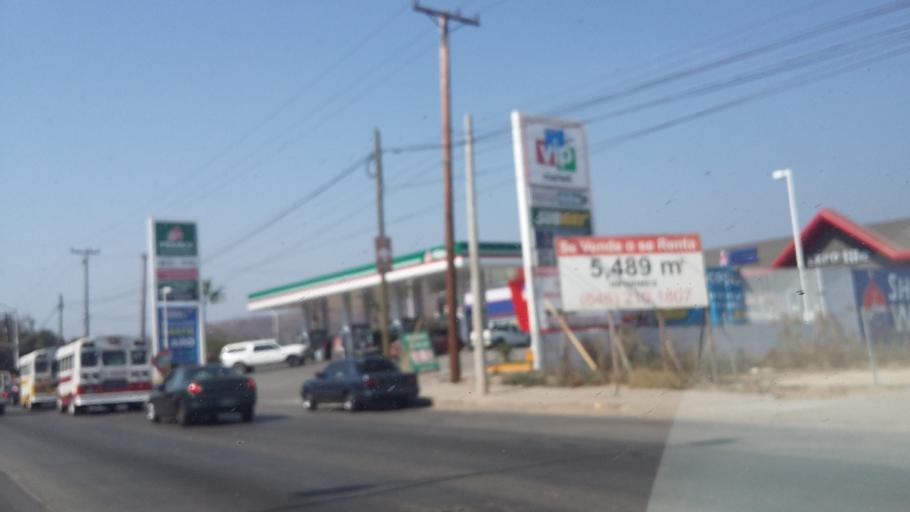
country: MX
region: Baja California
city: Ensenada
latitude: 31.8031
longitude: -116.5952
